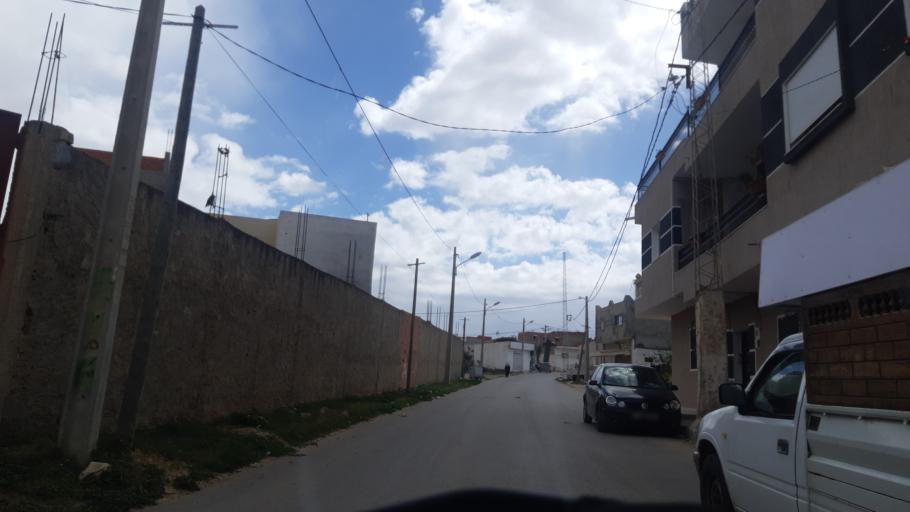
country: TN
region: Susah
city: Akouda
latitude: 35.8655
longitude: 10.5413
